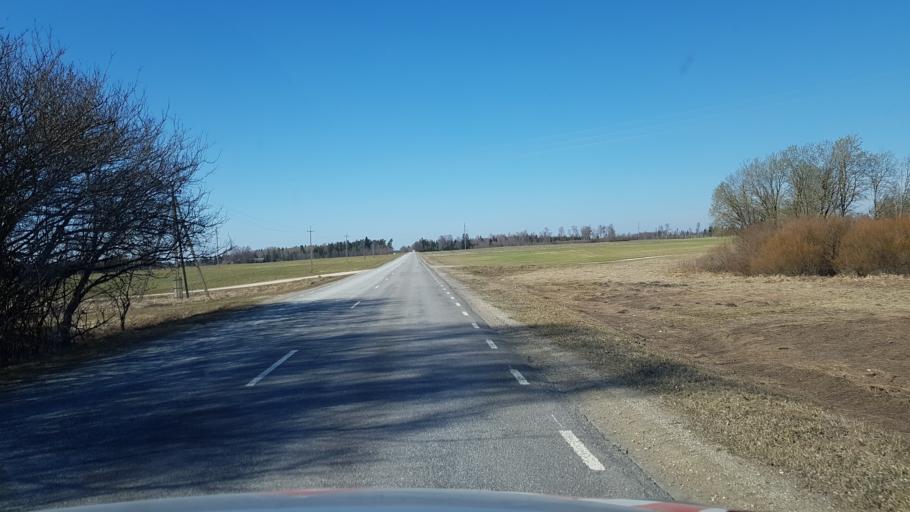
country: EE
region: Laeaene-Virumaa
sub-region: Vaeike-Maarja vald
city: Vaike-Maarja
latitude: 59.1455
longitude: 26.2301
